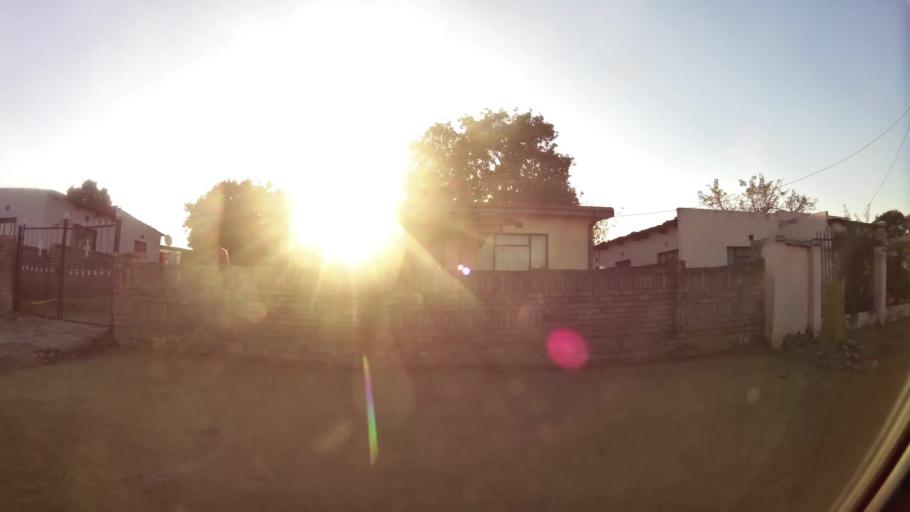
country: ZA
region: North-West
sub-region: Bojanala Platinum District Municipality
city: Rustenburg
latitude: -25.6425
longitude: 27.2168
